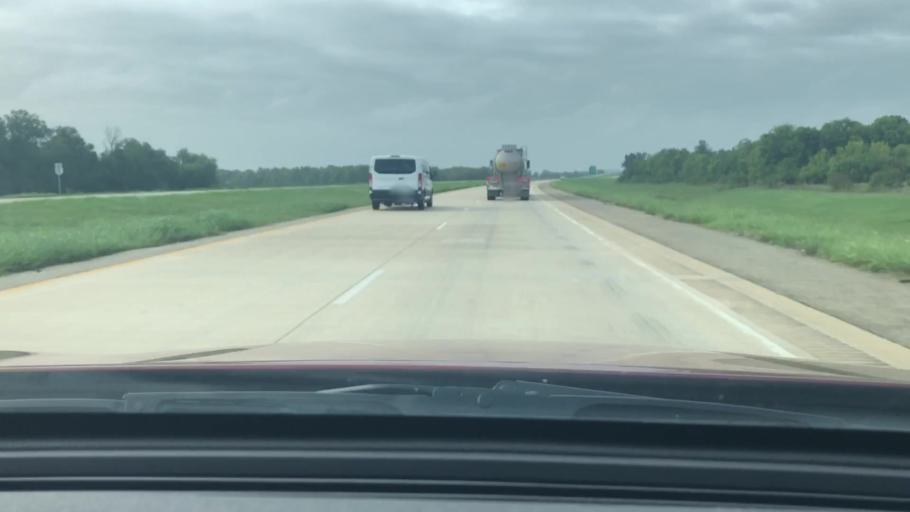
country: US
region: Louisiana
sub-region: Caddo Parish
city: Vivian
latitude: 32.8616
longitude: -93.8610
